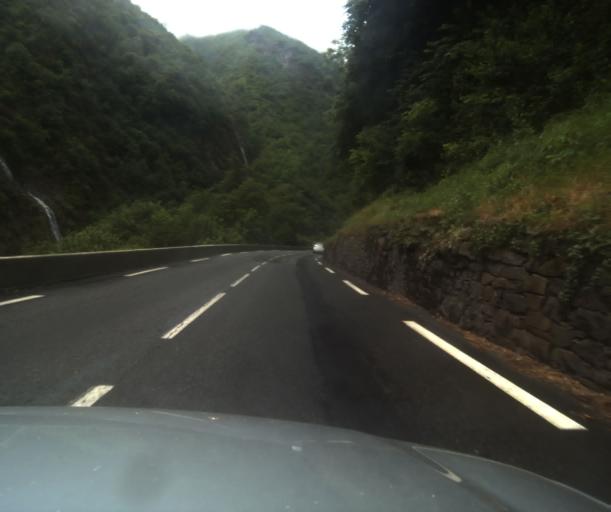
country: FR
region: Midi-Pyrenees
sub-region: Departement des Hautes-Pyrenees
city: Pierrefitte-Nestalas
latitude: 42.9301
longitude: -0.0449
